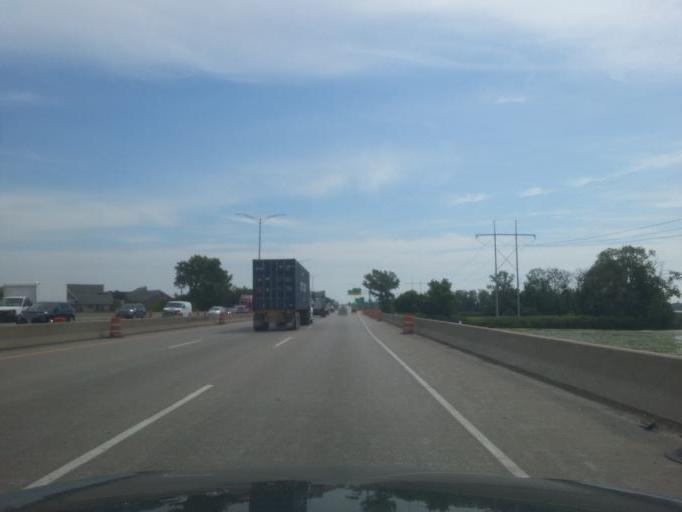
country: US
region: Wisconsin
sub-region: Dane County
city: Monona
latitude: 43.0444
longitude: -89.3302
